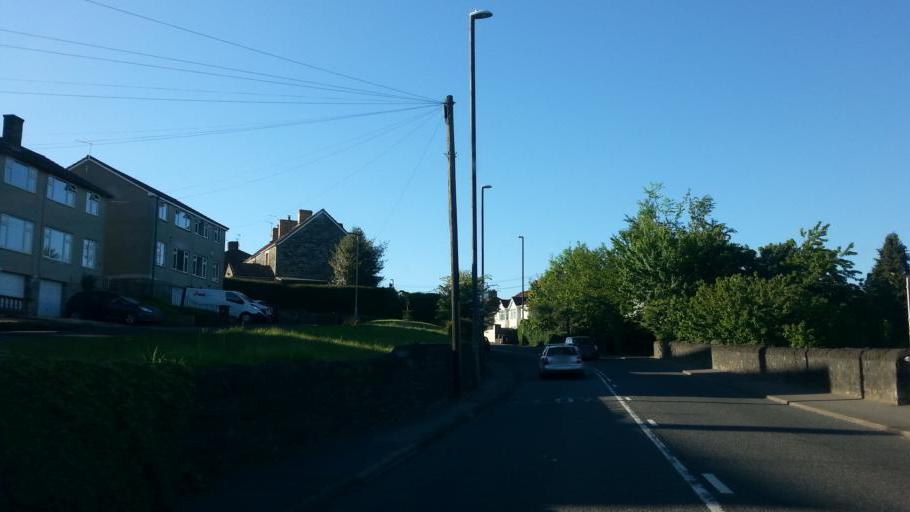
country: GB
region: England
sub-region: Bath and North East Somerset
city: Whitchurch
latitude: 51.4113
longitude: -2.5588
